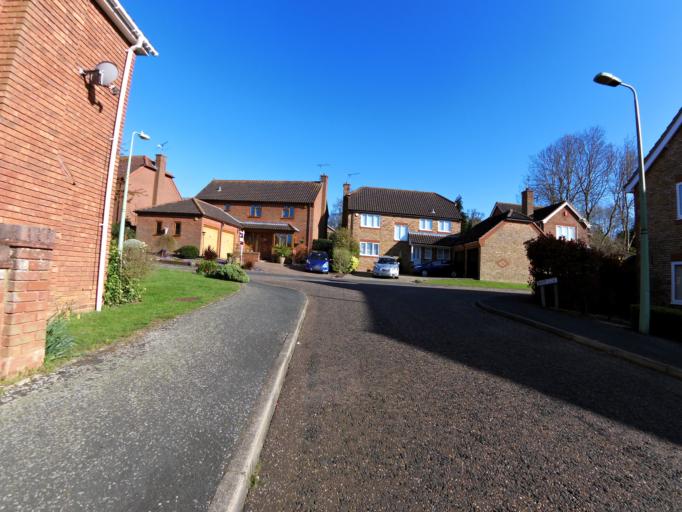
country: GB
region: England
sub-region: Suffolk
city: Bramford
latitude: 52.0568
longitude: 1.1151
